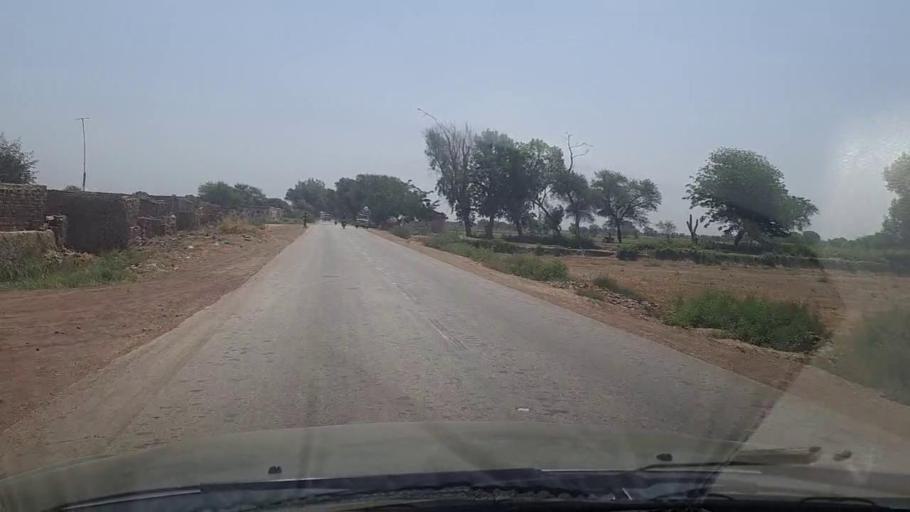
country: PK
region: Sindh
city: Hyderabad
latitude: 25.3777
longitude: 68.4580
